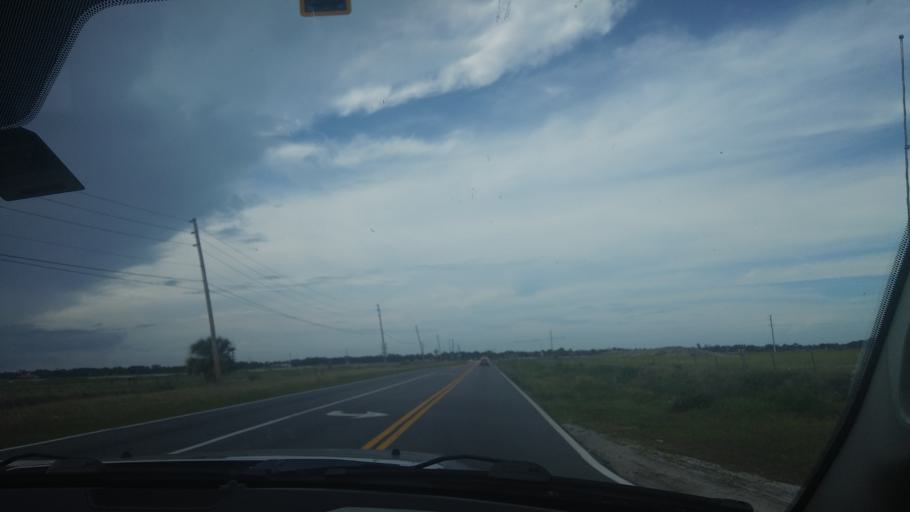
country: US
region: Florida
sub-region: Brevard County
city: Grant-Valkaria
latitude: 27.8976
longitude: -80.6223
